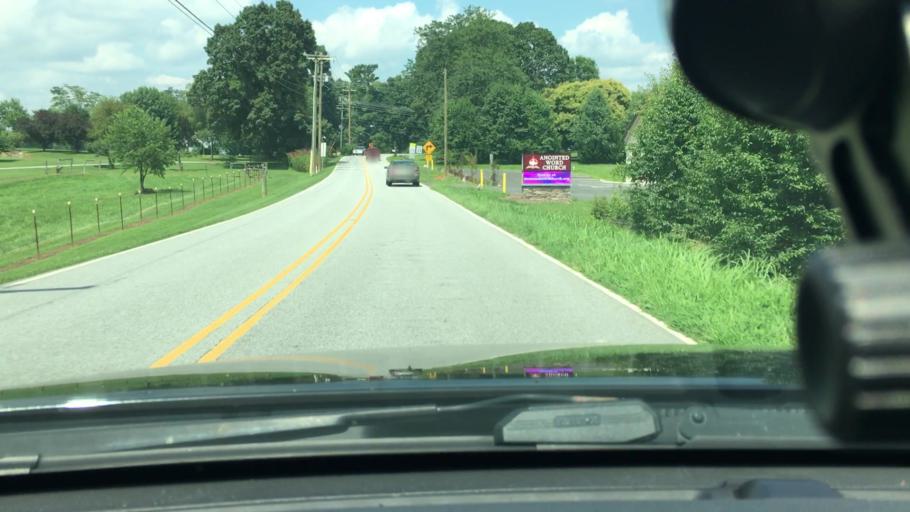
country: US
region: North Carolina
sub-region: Henderson County
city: Mills River
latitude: 35.4077
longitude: -82.5497
